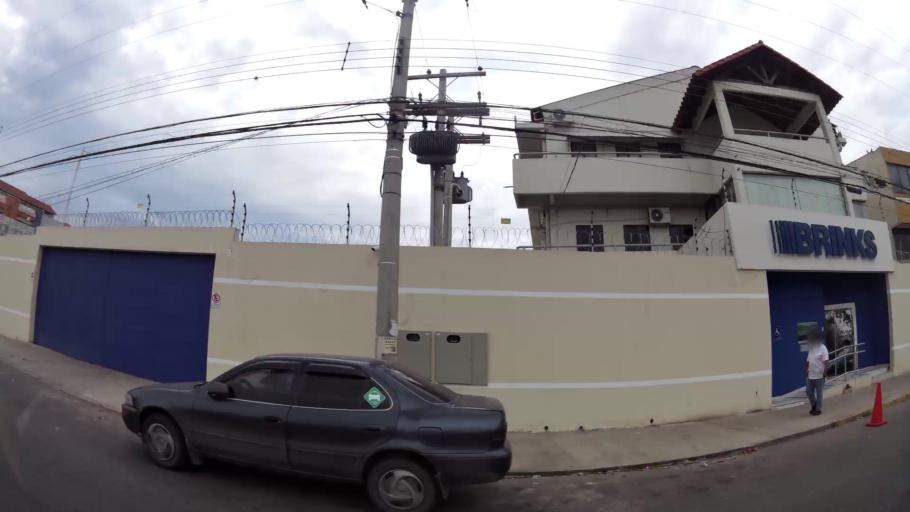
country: BO
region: Santa Cruz
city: Santa Cruz de la Sierra
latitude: -17.7659
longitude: -63.1619
